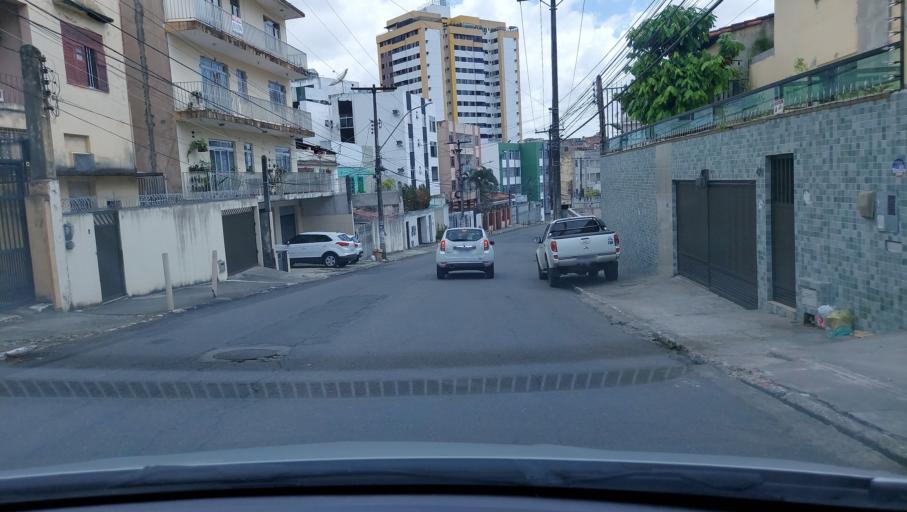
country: BR
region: Bahia
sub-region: Salvador
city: Salvador
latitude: -12.9699
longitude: -38.4896
